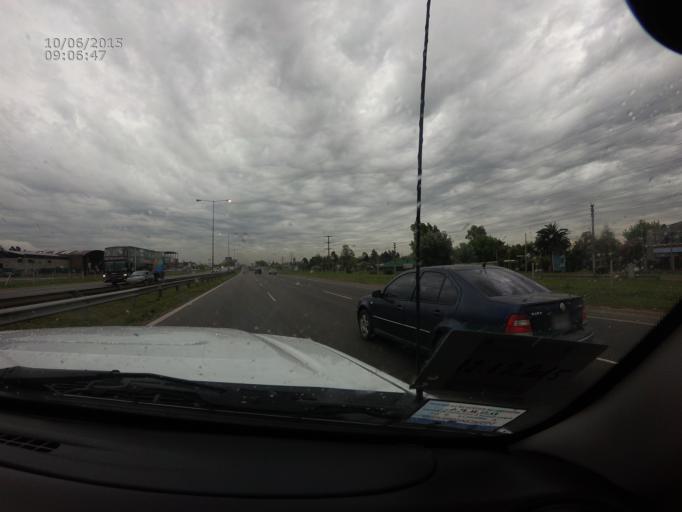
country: AR
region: Buenos Aires
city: Santa Catalina - Dique Lujan
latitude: -34.4119
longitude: -58.7270
